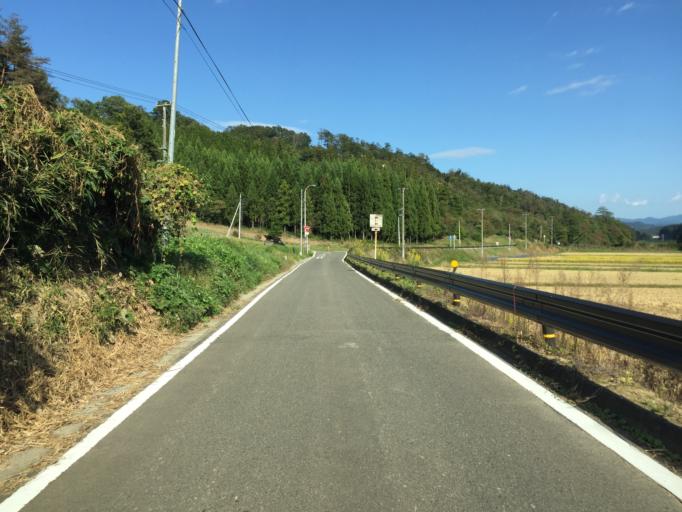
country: JP
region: Fukushima
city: Fukushima-shi
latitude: 37.6766
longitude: 140.4374
